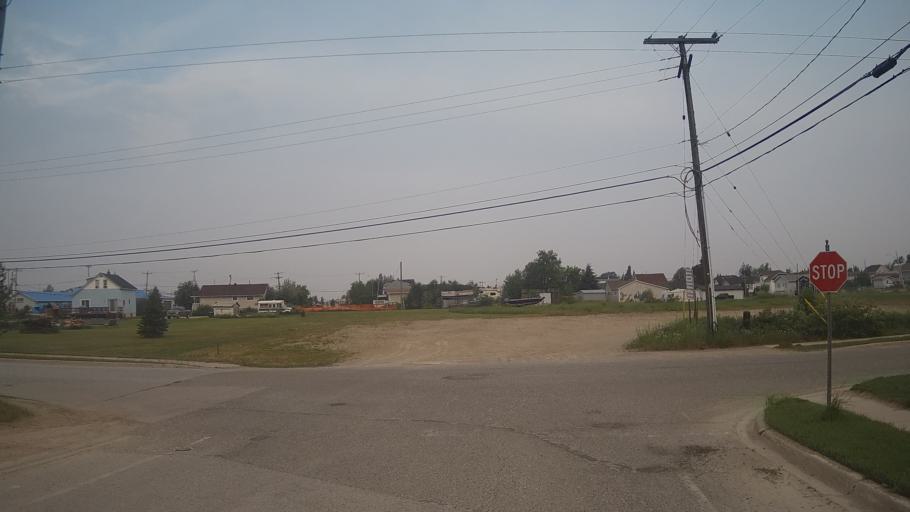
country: CA
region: Ontario
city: Hearst
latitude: 49.6899
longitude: -83.6537
